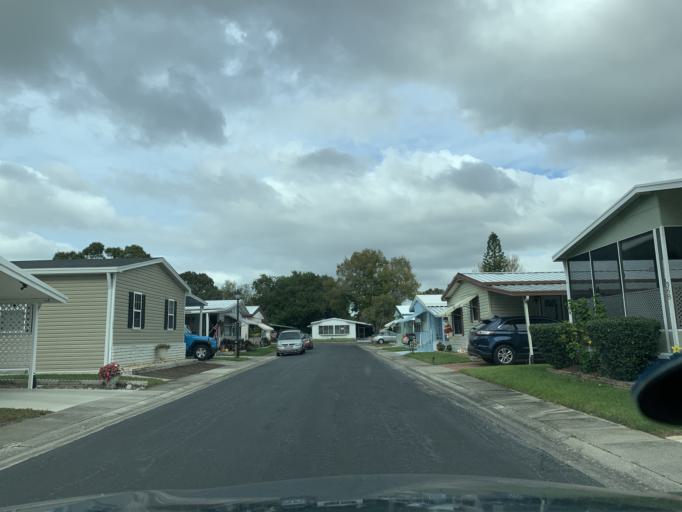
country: US
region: Florida
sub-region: Pinellas County
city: Ridgecrest
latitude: 27.8810
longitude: -82.7936
